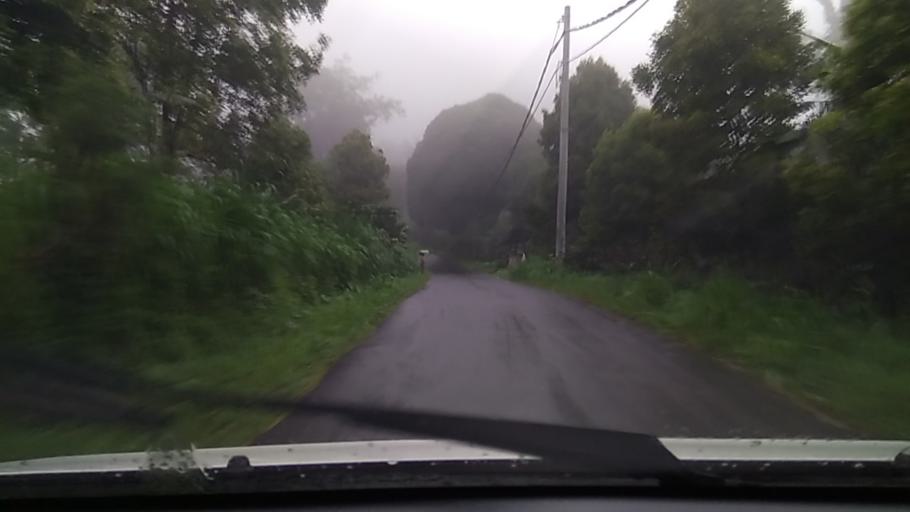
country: ID
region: Bali
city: Banjar Ambengan
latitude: -8.2024
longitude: 115.1747
